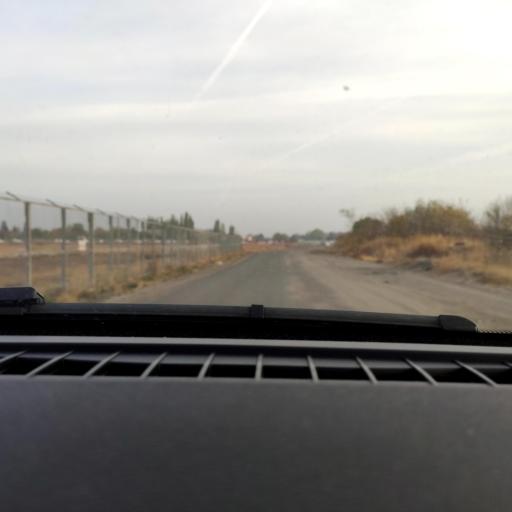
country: RU
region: Voronezj
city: Voronezh
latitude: 51.6611
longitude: 39.2684
